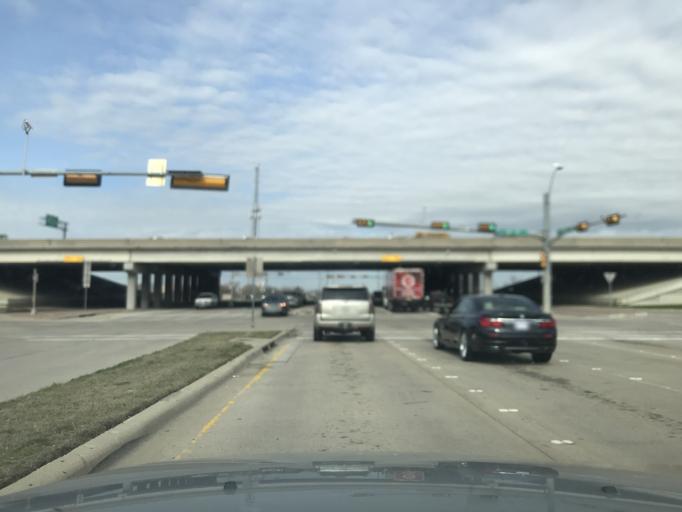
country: US
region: Texas
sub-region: Denton County
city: The Colony
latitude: 33.0818
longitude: -96.8517
